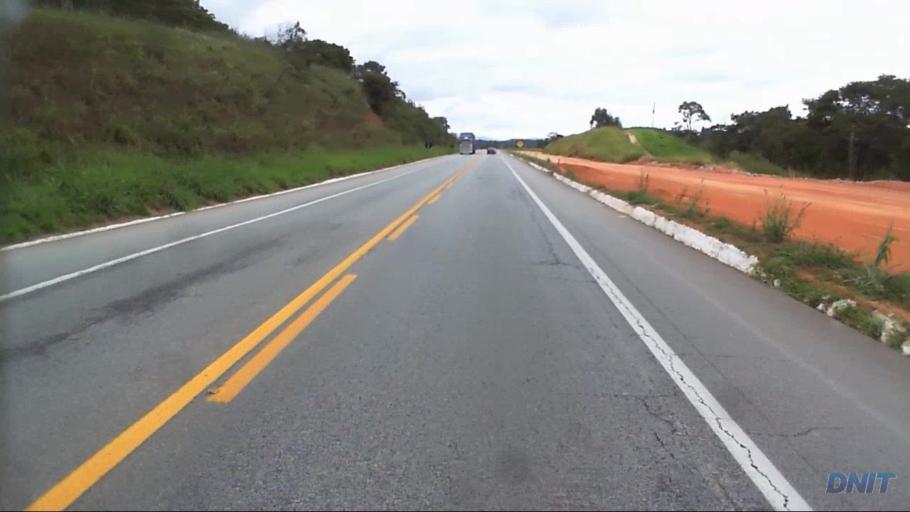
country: BR
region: Minas Gerais
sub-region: Barao De Cocais
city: Barao de Cocais
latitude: -19.7655
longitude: -43.4591
